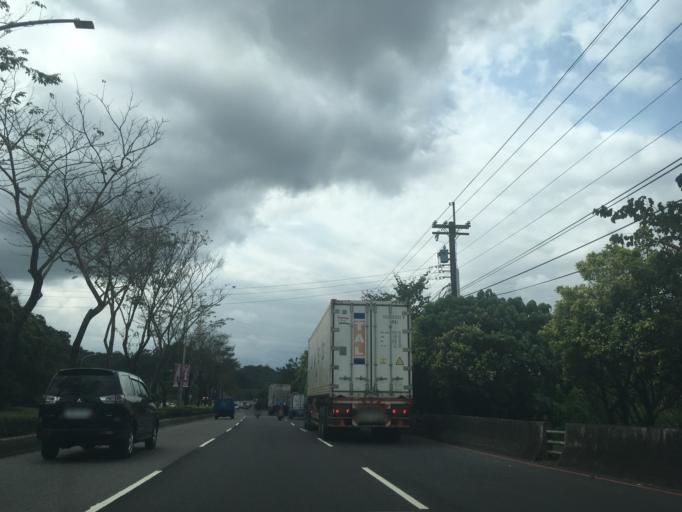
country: TW
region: Taipei
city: Taipei
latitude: 25.0596
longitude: 121.6440
